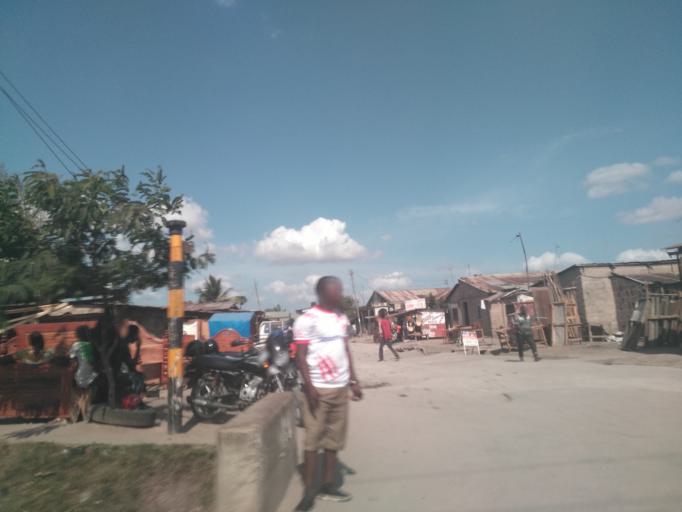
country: TZ
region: Dar es Salaam
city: Dar es Salaam
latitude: -6.8692
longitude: 39.2559
